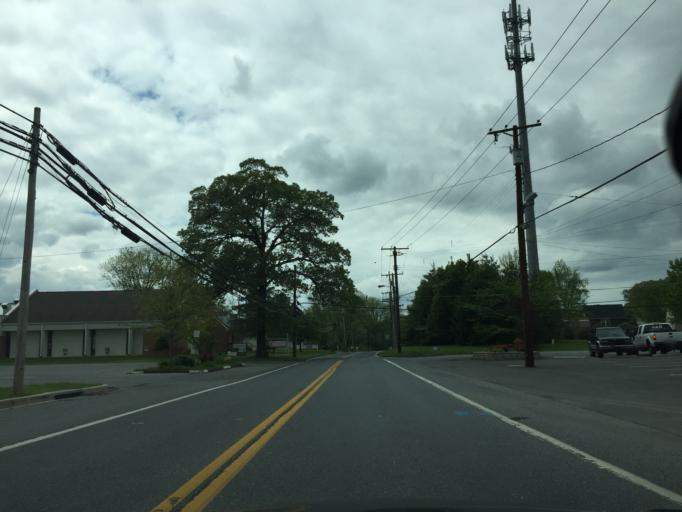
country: US
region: Maryland
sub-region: Baltimore County
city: Middle River
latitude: 39.2947
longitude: -76.4311
